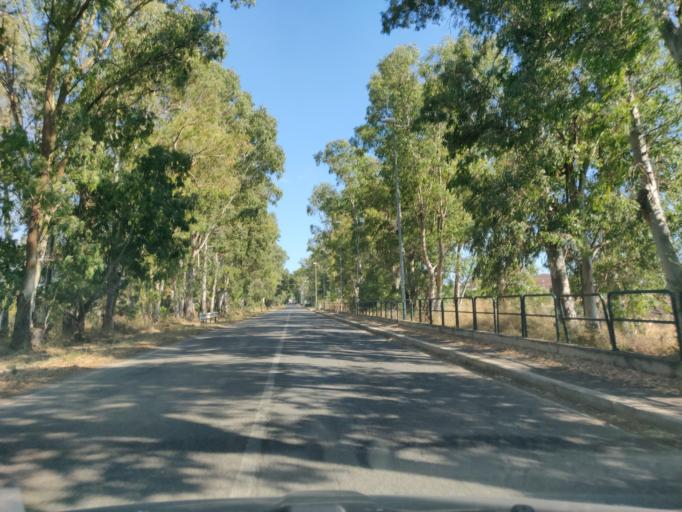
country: IT
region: Latium
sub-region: Citta metropolitana di Roma Capitale
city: Aurelia
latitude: 42.1485
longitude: 11.7604
